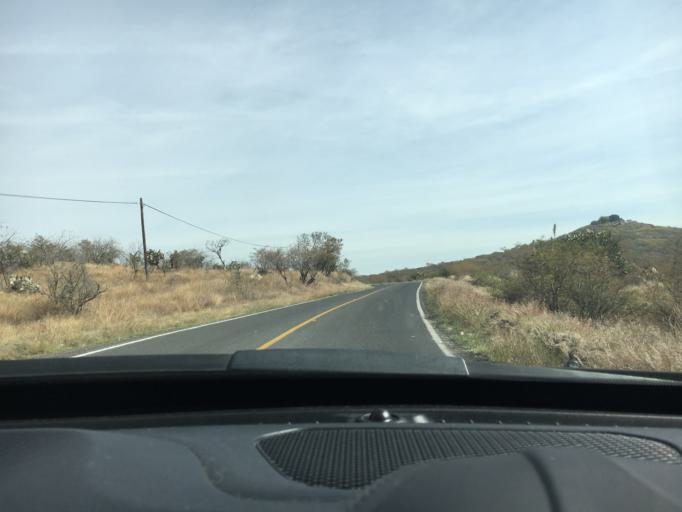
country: MX
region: Guanajuato
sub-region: Silao de la Victoria
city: San Francisco (Banos de Agua Caliente)
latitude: 21.0628
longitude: -101.5026
